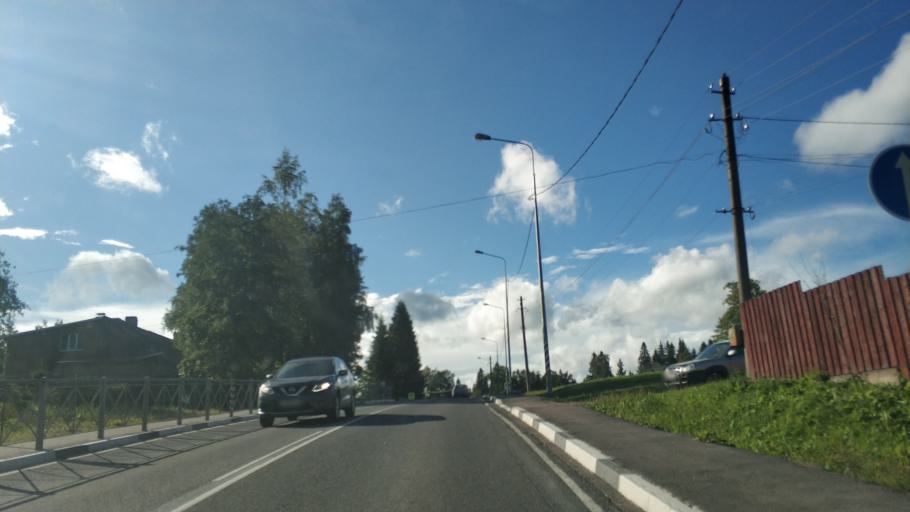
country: RU
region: Republic of Karelia
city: Lakhdenpokh'ya
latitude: 61.5223
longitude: 30.1859
